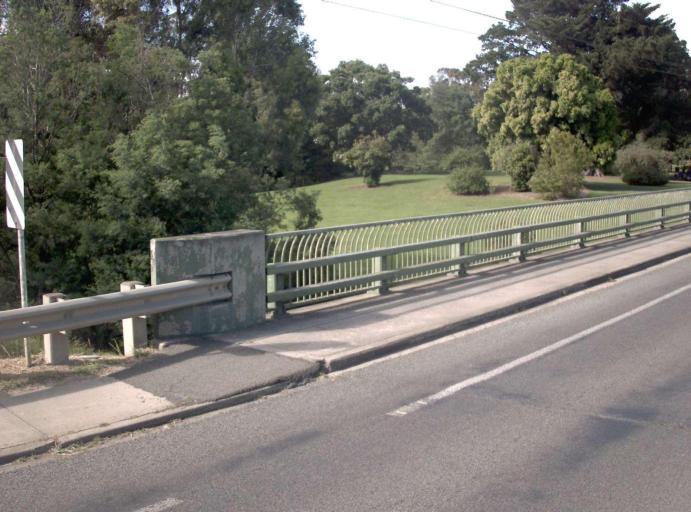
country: AU
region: Victoria
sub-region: Latrobe
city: Traralgon
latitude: -38.1939
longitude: 146.5439
